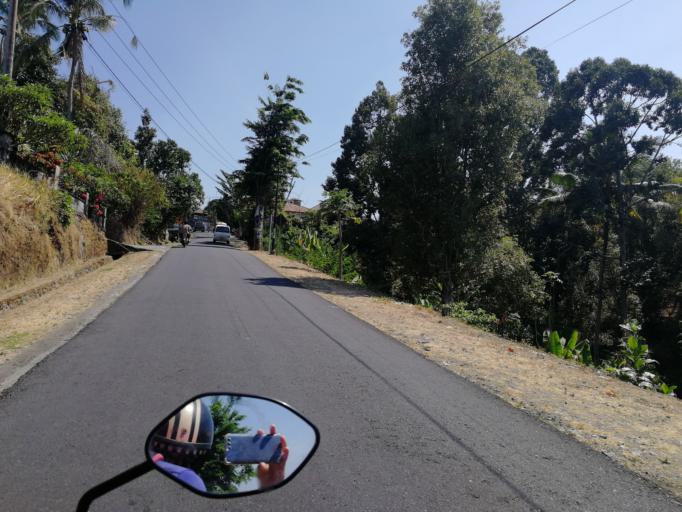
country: ID
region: Bali
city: Banjar Kedisan
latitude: -8.1479
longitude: 115.3065
